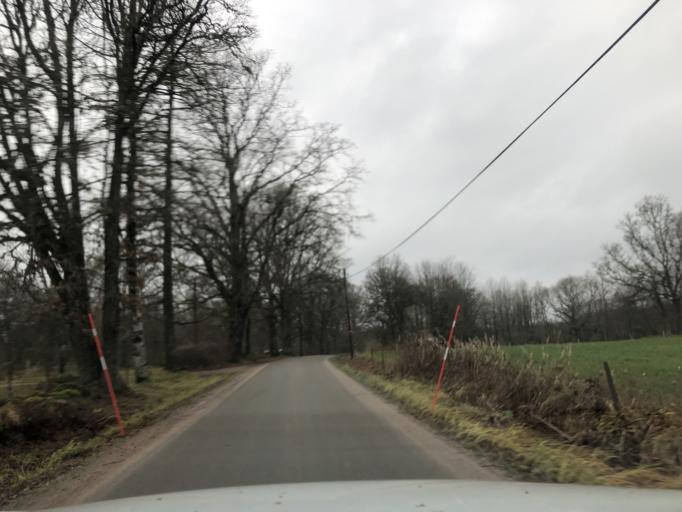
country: SE
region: Vaestra Goetaland
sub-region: Ulricehamns Kommun
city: Ulricehamn
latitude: 57.8610
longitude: 13.5858
